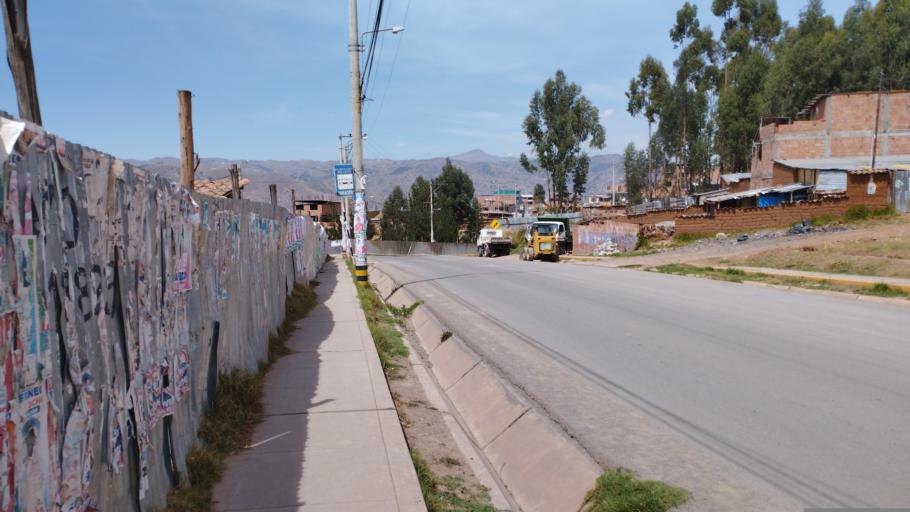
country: PE
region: Cusco
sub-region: Provincia de Cusco
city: Cusco
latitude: -13.5230
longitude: -71.9206
